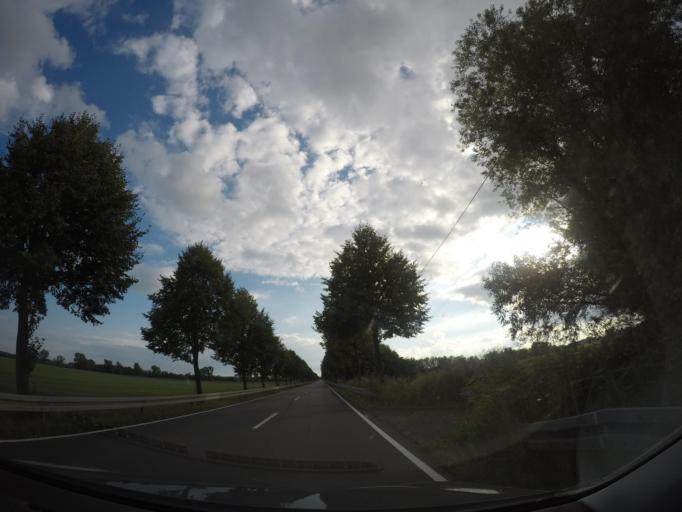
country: DE
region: Saxony-Anhalt
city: Mieste
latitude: 52.4220
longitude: 11.1302
